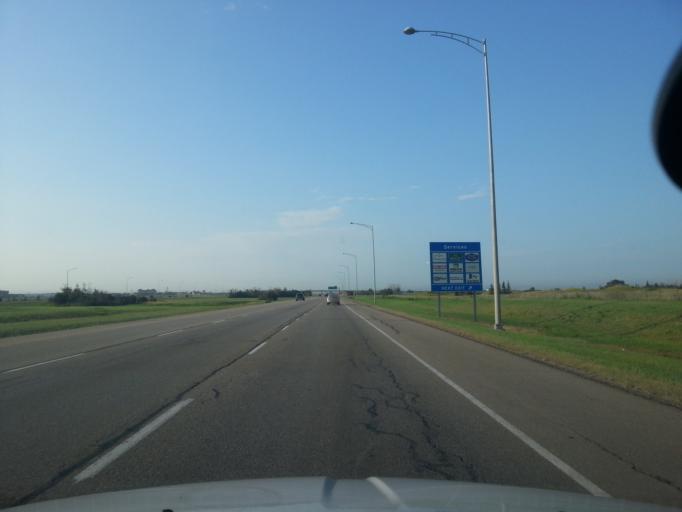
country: CA
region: Alberta
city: Leduc
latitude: 53.3217
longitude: -113.5500
